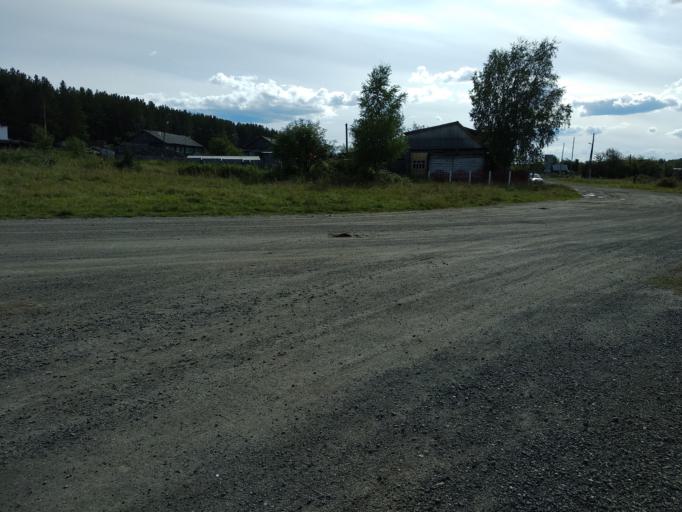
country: RU
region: Sverdlovsk
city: Krasnotur'insk
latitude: 59.9198
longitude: 60.3015
